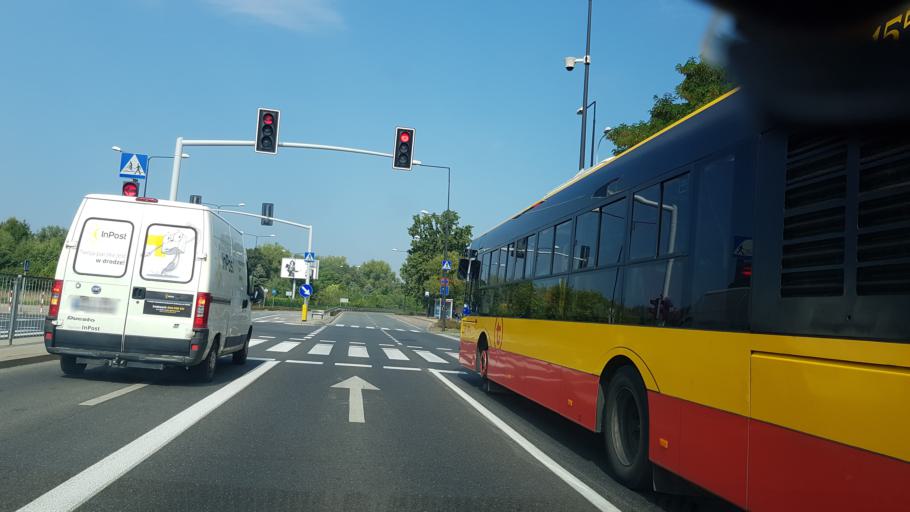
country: PL
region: Masovian Voivodeship
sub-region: Warszawa
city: Ursynow
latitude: 52.1647
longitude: 21.0459
